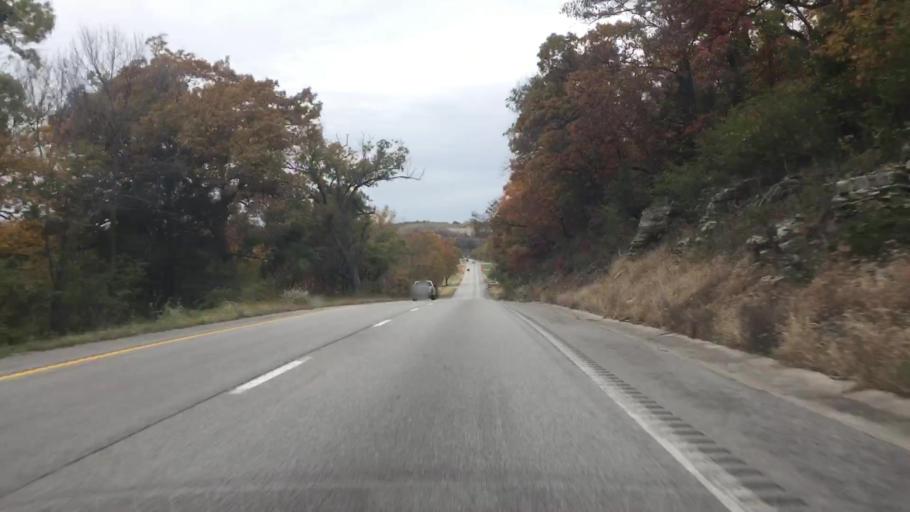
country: US
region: Missouri
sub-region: Jackson County
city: Lees Summit
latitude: 38.9571
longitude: -94.4207
